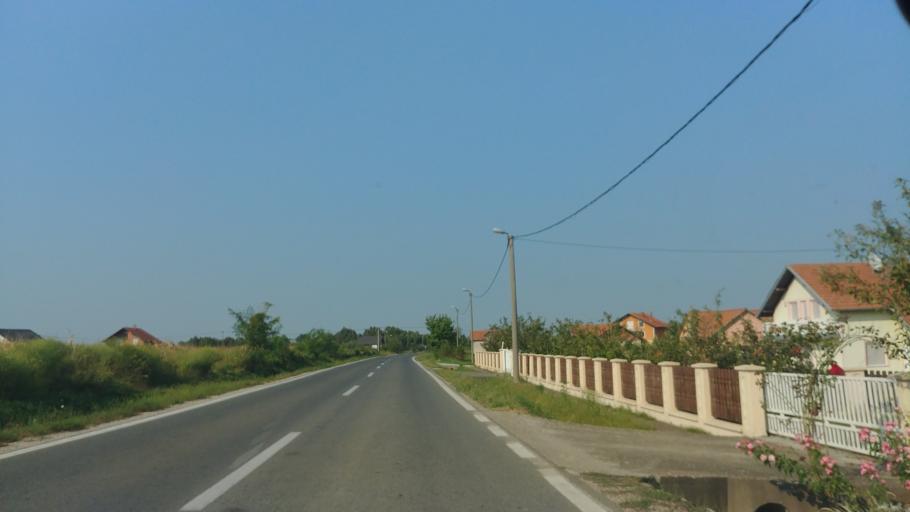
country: BA
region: Brcko
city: Brcko
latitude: 44.7803
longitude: 18.8111
